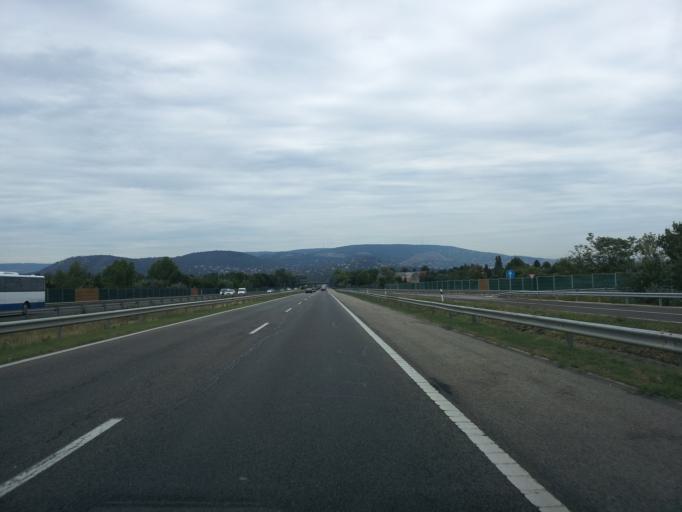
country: HU
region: Pest
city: Toeroekbalint
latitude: 47.4349
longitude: 18.8984
